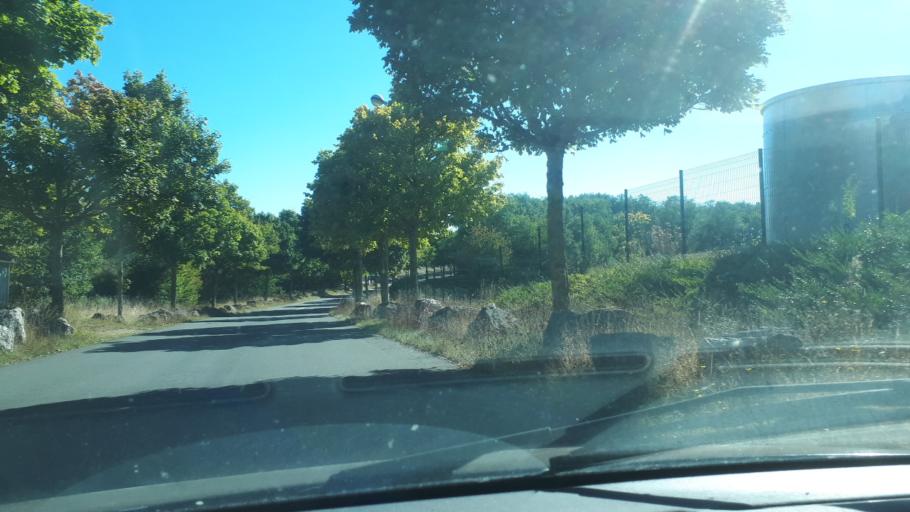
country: FR
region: Centre
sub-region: Departement du Loir-et-Cher
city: Naveil
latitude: 47.8145
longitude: 1.0249
